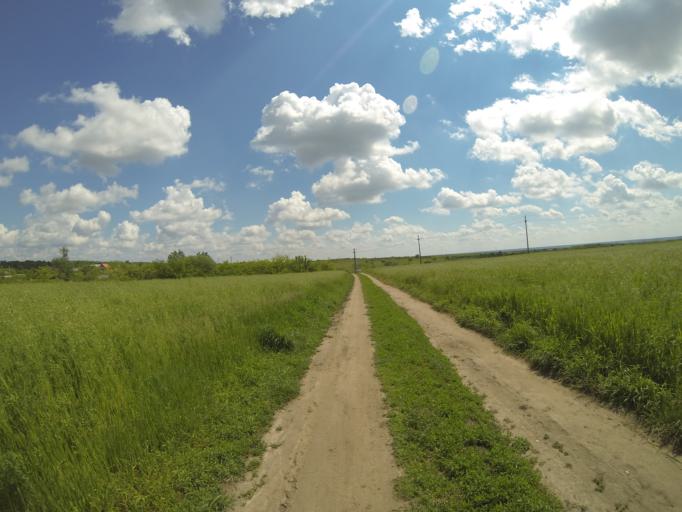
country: RO
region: Dolj
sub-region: Comuna Carcea
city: Carcea
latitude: 44.2688
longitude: 23.8807
